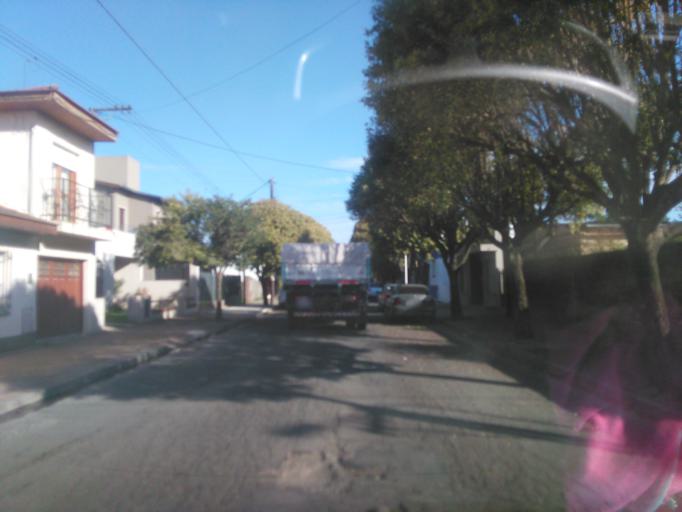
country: AR
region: Buenos Aires
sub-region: Partido de Tandil
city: Tandil
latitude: -37.3284
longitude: -59.1263
